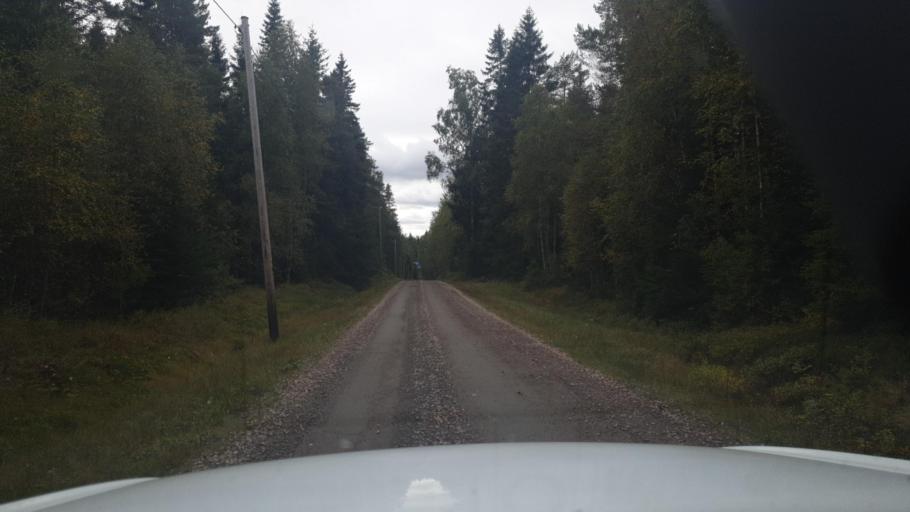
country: SE
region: Vaermland
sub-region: Eda Kommun
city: Charlottenberg
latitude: 60.1555
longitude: 12.5991
